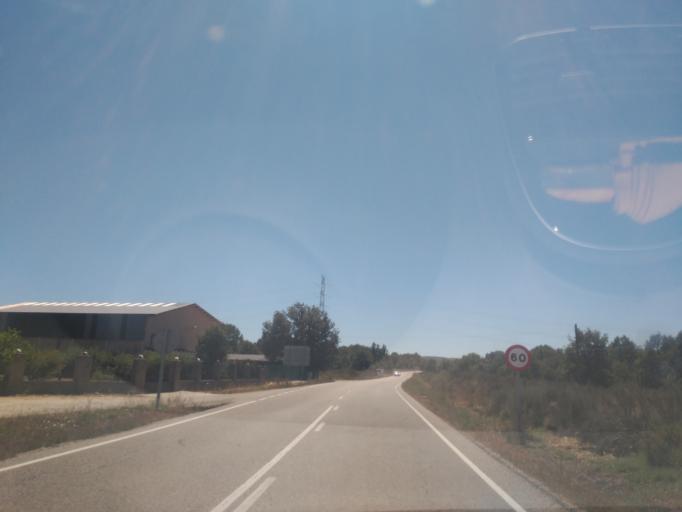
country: ES
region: Castille and Leon
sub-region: Provincia de Zamora
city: Puebla de Sanabria
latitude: 42.0697
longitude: -6.6214
